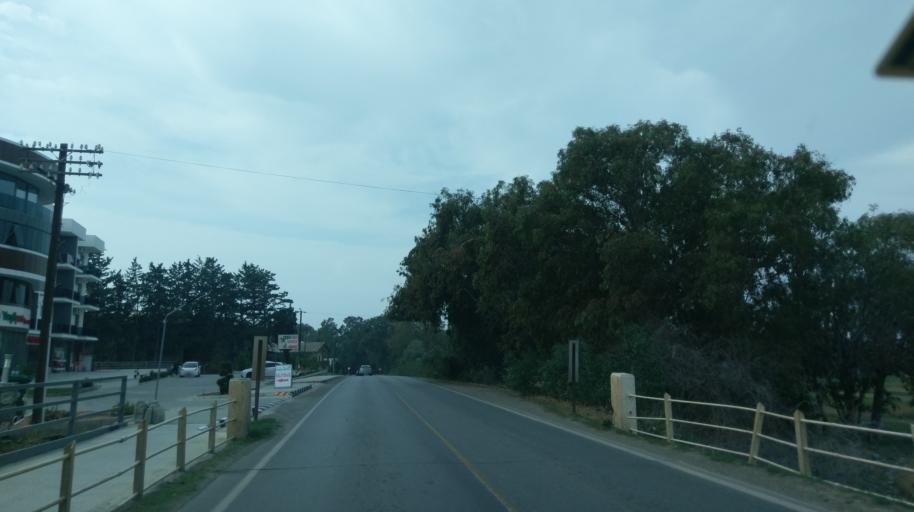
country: CY
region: Lefkosia
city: Lefka
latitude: 35.1548
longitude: 32.8700
